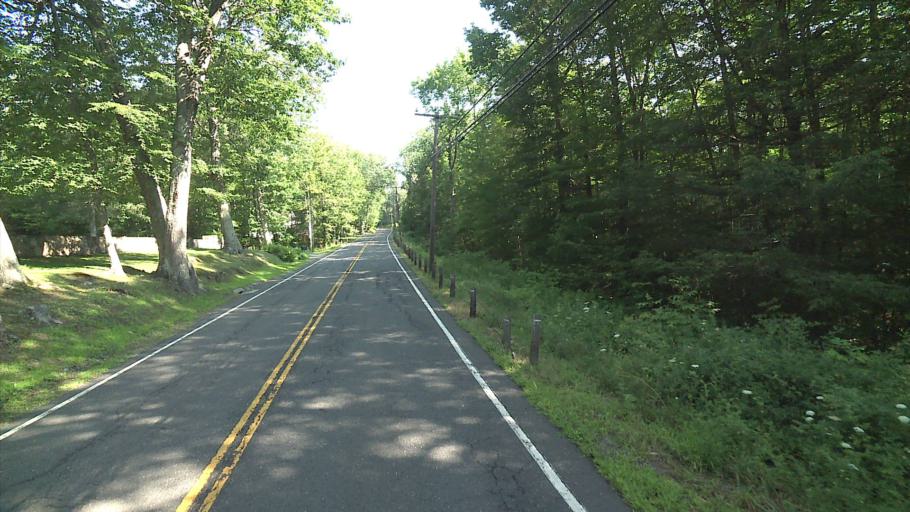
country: US
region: Connecticut
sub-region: Litchfield County
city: Winsted
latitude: 41.9674
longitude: -73.1040
